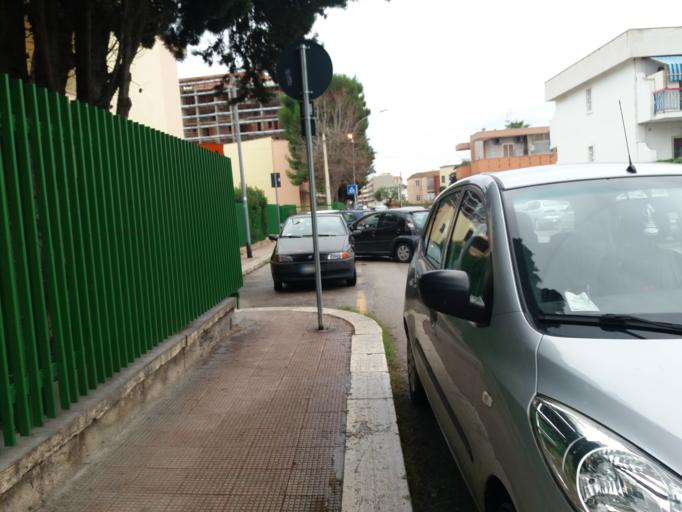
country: IT
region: Apulia
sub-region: Provincia di Bari
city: San Paolo
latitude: 41.1363
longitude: 16.8204
